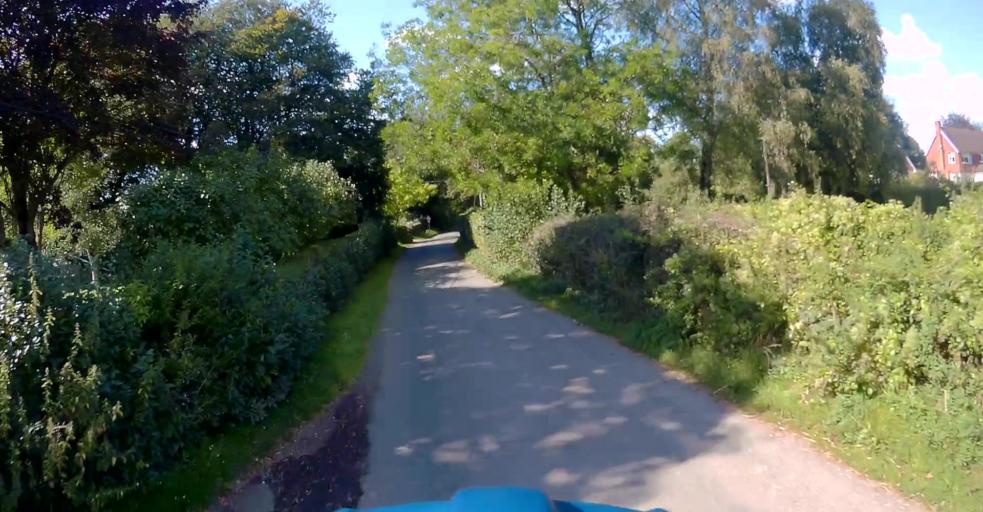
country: GB
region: England
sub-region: Hampshire
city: Four Marks
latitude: 51.1695
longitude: -1.0926
